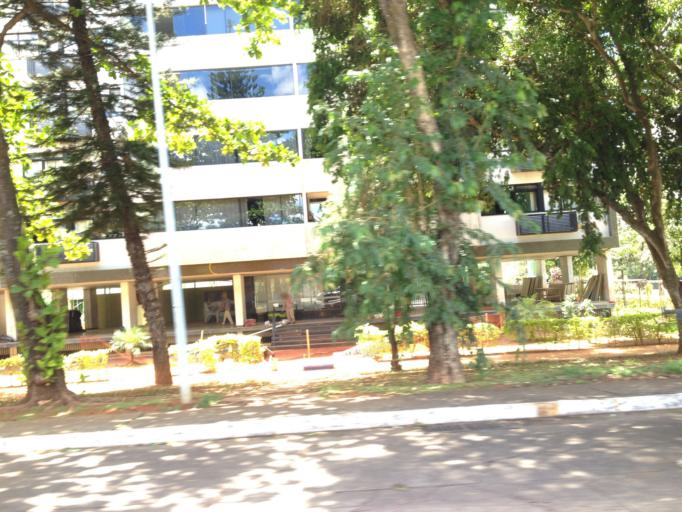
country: BR
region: Federal District
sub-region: Brasilia
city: Brasilia
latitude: -15.8276
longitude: -47.9261
